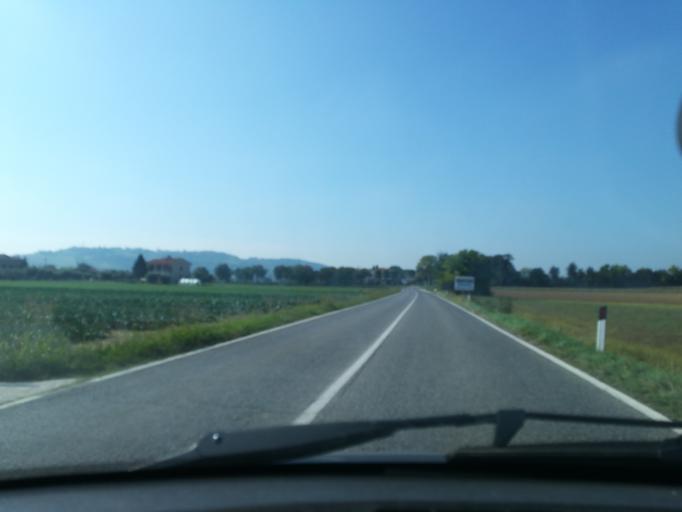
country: IT
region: The Marches
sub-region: Provincia di Macerata
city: Zona Industriale
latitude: 43.2668
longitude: 13.4600
